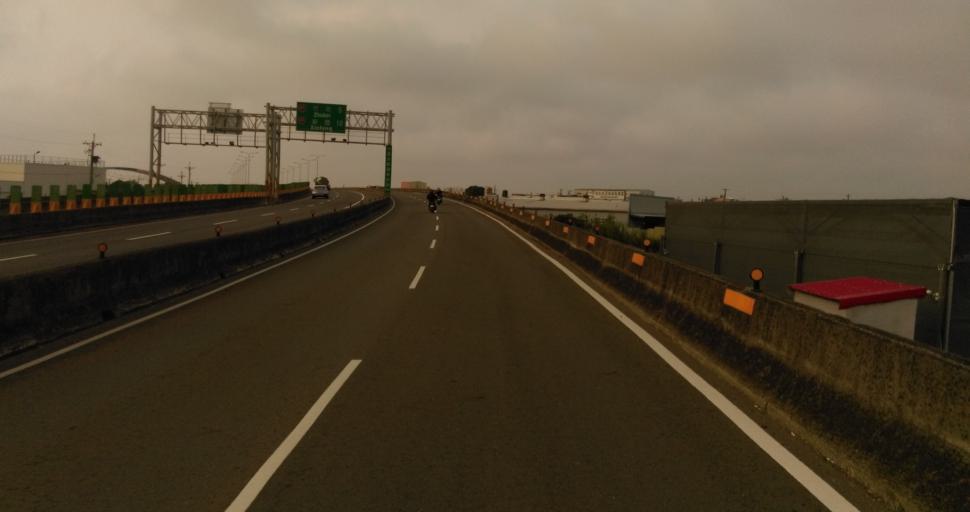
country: TW
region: Taiwan
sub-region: Hsinchu
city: Hsinchu
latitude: 24.8020
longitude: 120.9206
